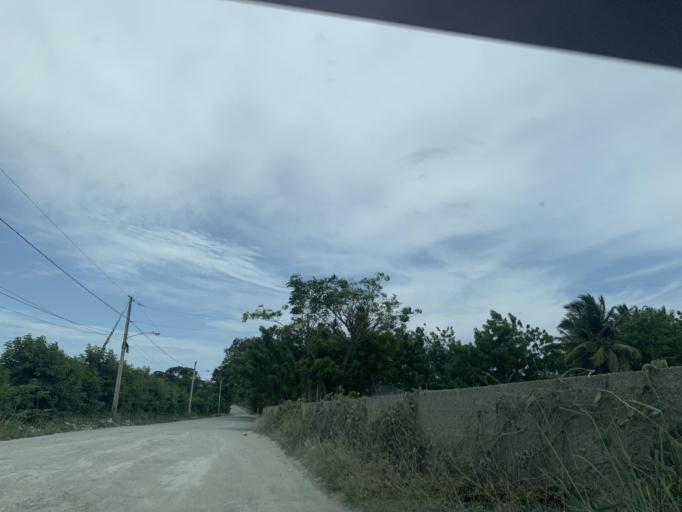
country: DO
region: Puerto Plata
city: Imbert
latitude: 19.8225
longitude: -70.7839
